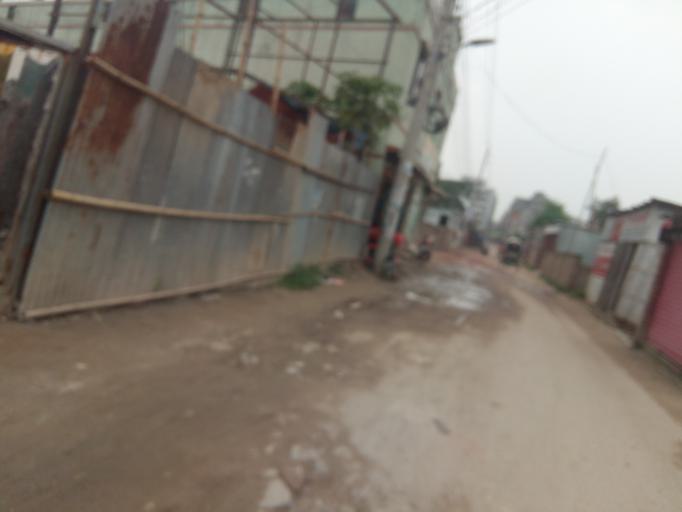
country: BD
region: Dhaka
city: Paltan
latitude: 23.7569
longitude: 90.4294
